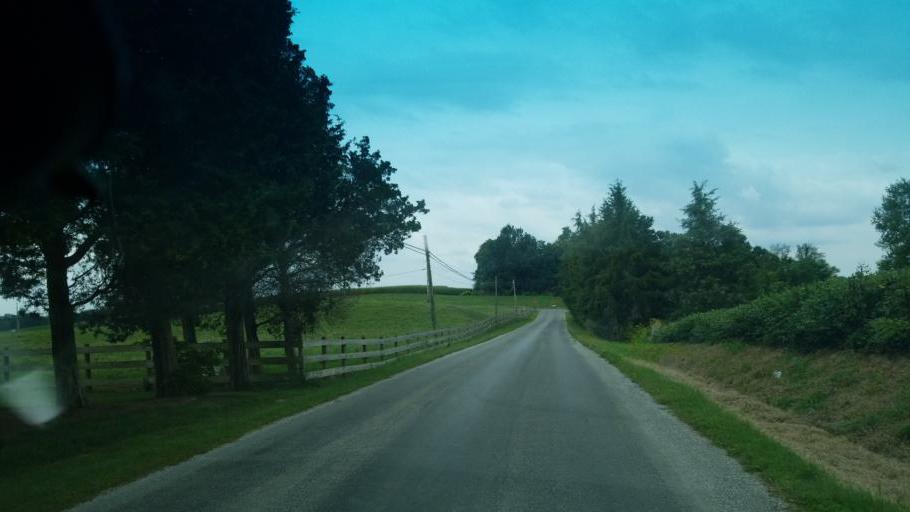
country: US
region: Ohio
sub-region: Richland County
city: Shelby
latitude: 40.9400
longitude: -82.6001
